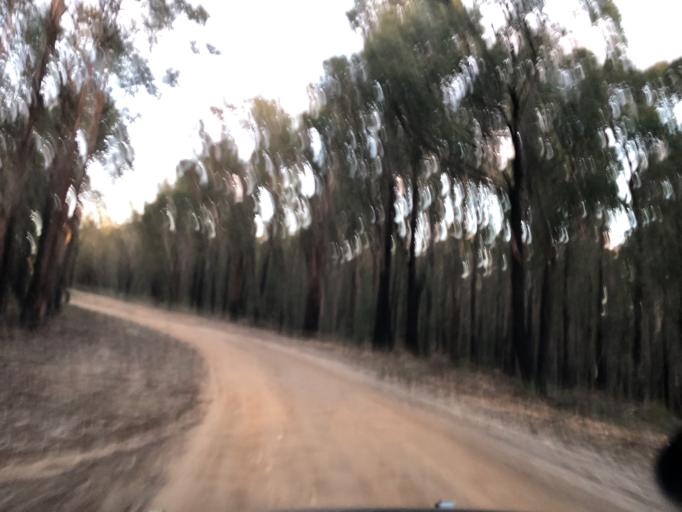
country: AU
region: Victoria
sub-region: Moorabool
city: Bacchus Marsh
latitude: -37.4747
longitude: 144.4235
